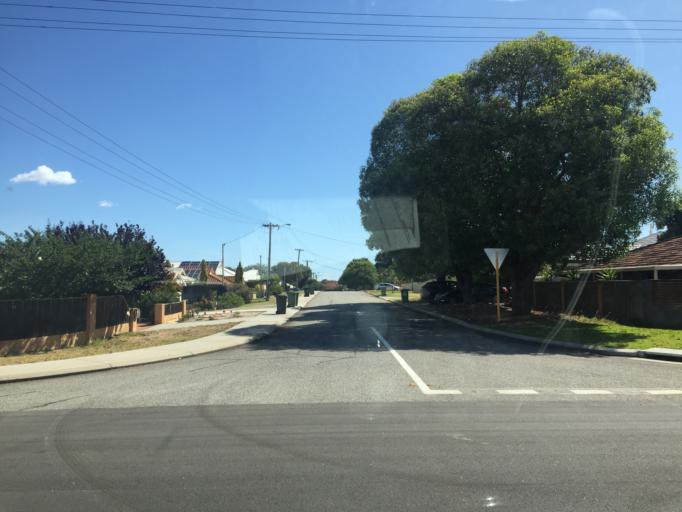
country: AU
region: Western Australia
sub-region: Belmont
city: Redcliffe
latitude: -31.9358
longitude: 115.9378
